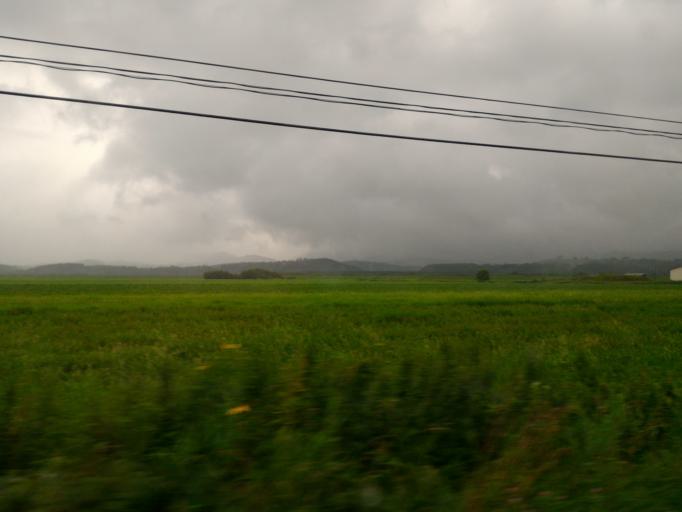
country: JP
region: Hokkaido
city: Makubetsu
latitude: 44.8264
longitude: 142.0628
